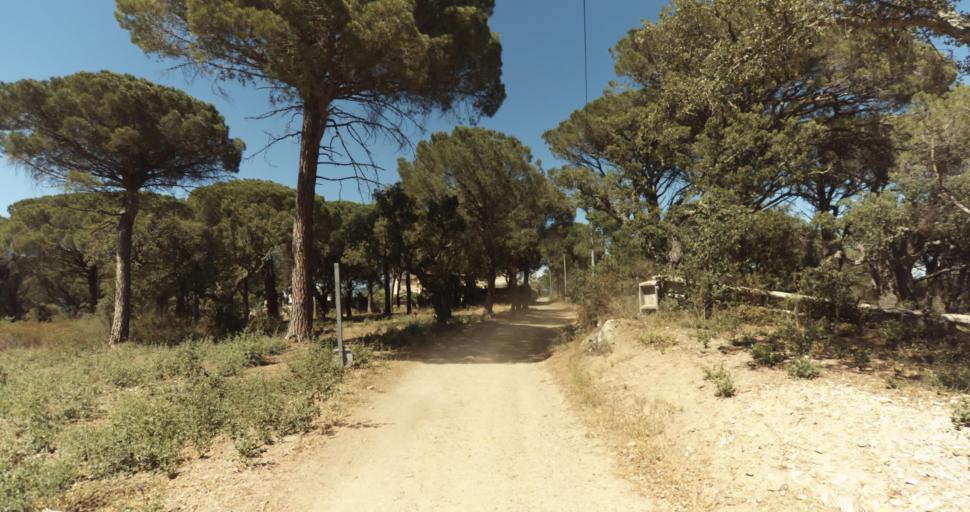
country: FR
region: Provence-Alpes-Cote d'Azur
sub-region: Departement du Var
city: Gassin
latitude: 43.2544
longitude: 6.5651
